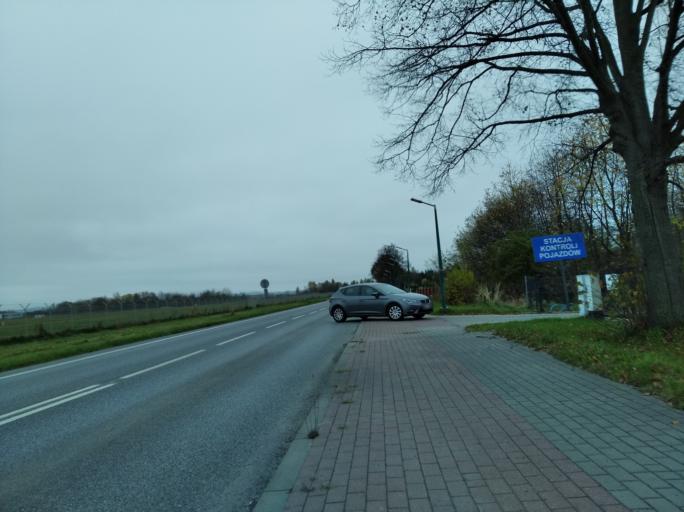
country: PL
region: Subcarpathian Voivodeship
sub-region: Krosno
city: Krosno
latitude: 49.6858
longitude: 21.7241
